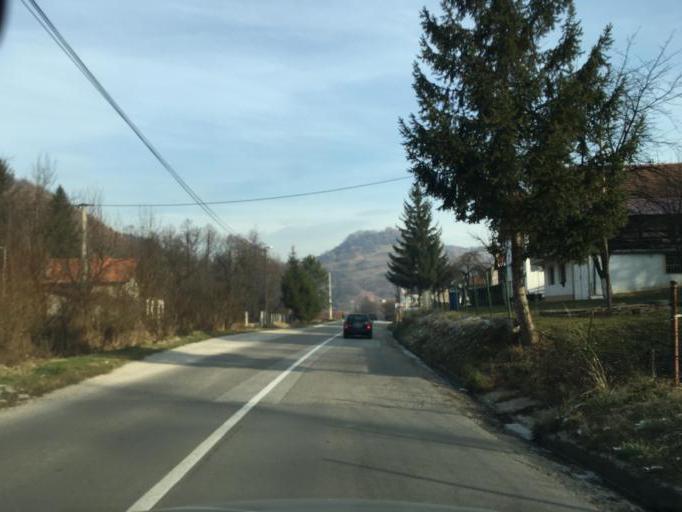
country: BA
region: Federation of Bosnia and Herzegovina
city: Lokvine
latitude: 44.1871
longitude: 17.8530
